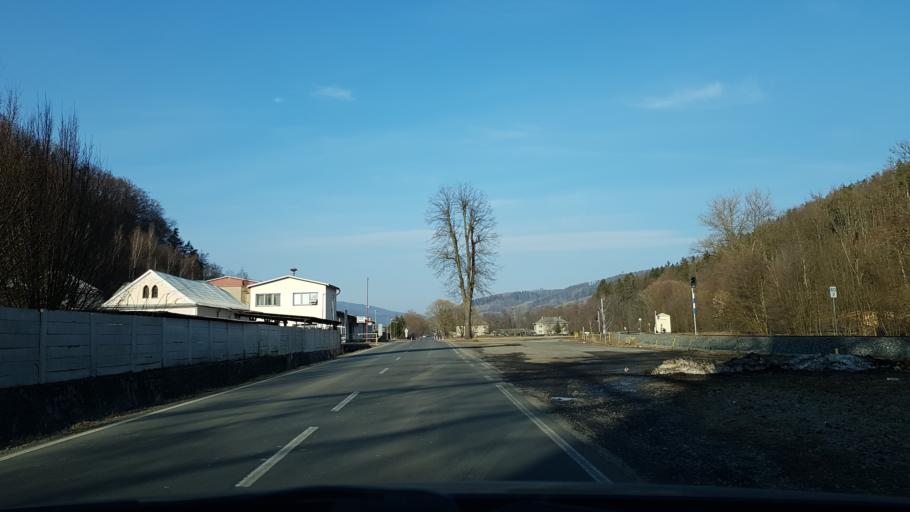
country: CZ
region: Olomoucky
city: Ruda nad Moravou
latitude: 49.9904
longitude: 16.8918
